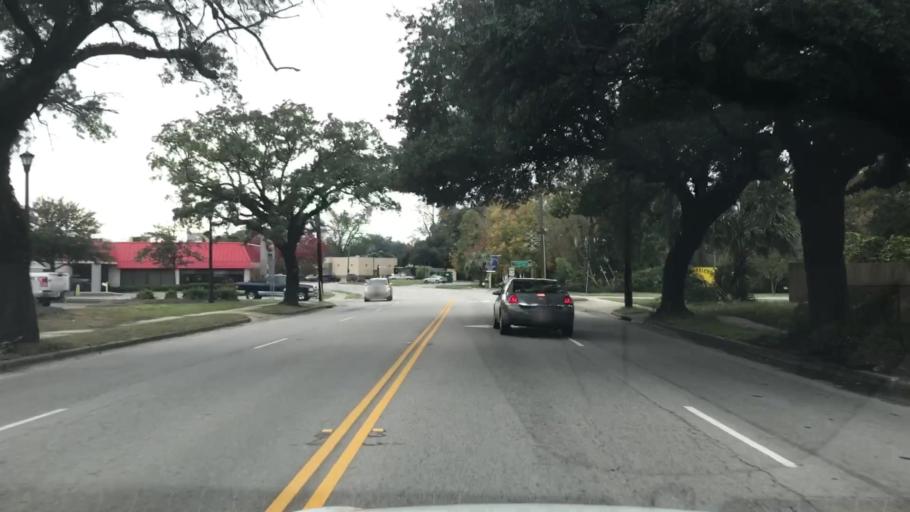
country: US
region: South Carolina
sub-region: Georgetown County
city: Georgetown
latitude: 33.3748
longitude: -79.2848
